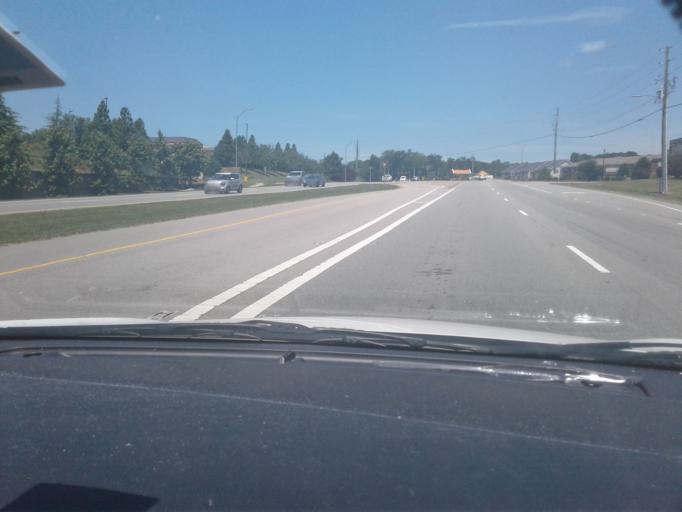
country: US
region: North Carolina
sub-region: Wake County
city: Holly Springs
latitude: 35.6361
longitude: -78.8298
